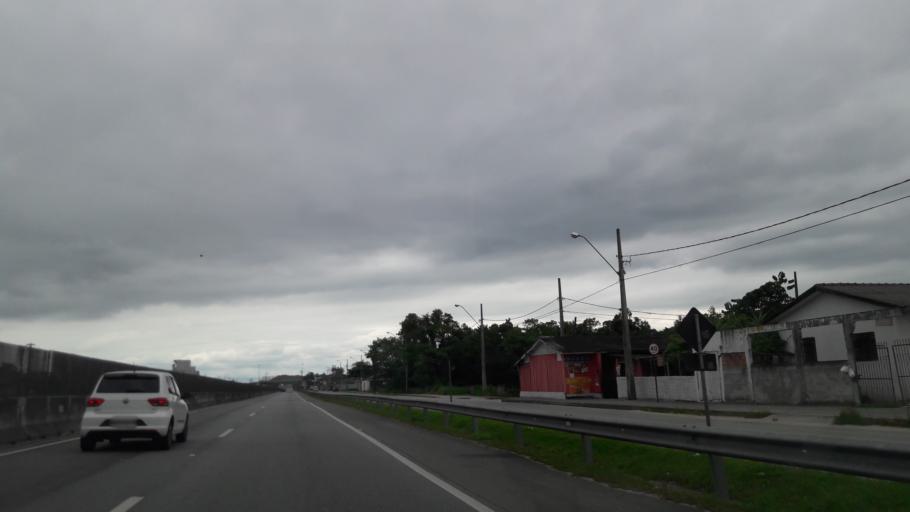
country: BR
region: Parana
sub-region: Paranagua
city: Paranagua
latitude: -25.5799
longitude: -48.5707
